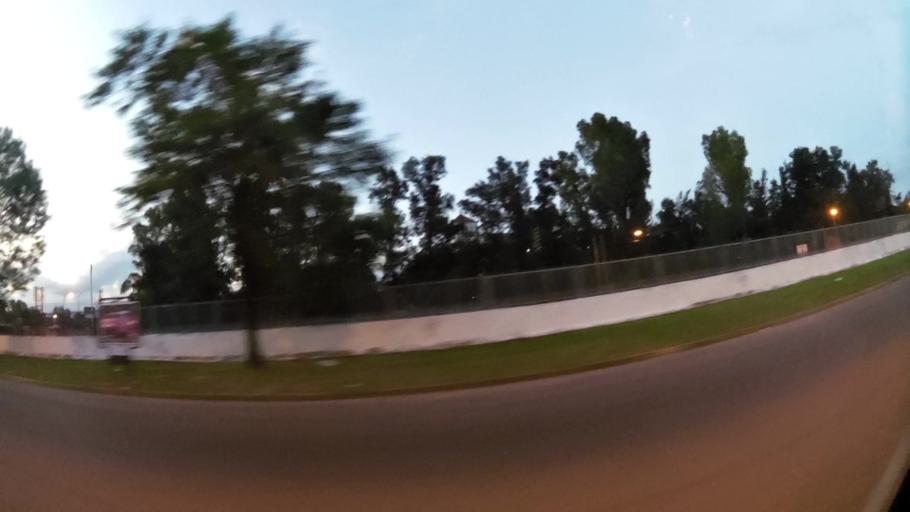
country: AR
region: Buenos Aires
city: Ituzaingo
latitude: -34.6631
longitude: -58.6770
